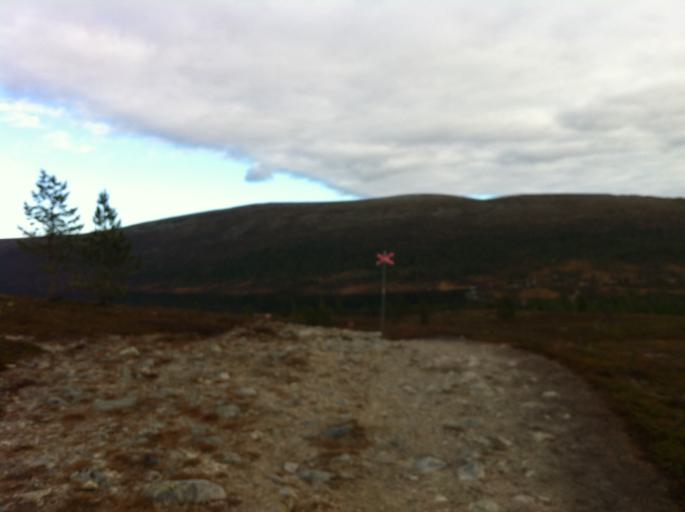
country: NO
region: Hedmark
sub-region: Engerdal
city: Engerdal
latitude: 62.1032
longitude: 12.2784
